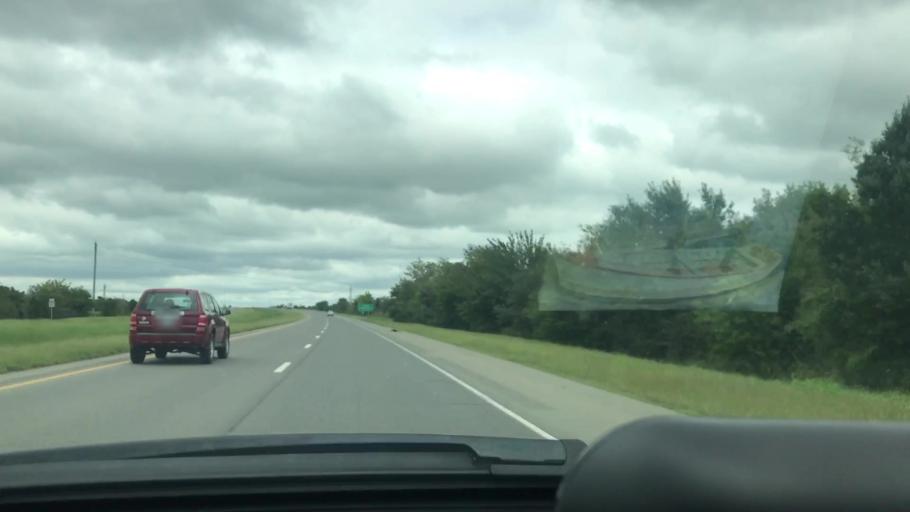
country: US
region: Oklahoma
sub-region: McIntosh County
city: Checotah
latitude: 35.5670
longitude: -95.4916
